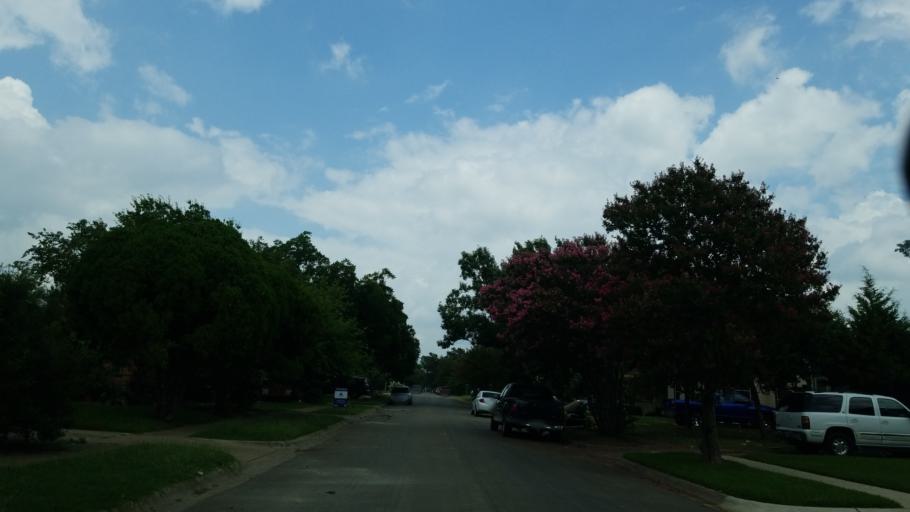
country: US
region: Texas
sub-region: Dallas County
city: University Park
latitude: 32.8486
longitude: -96.8347
